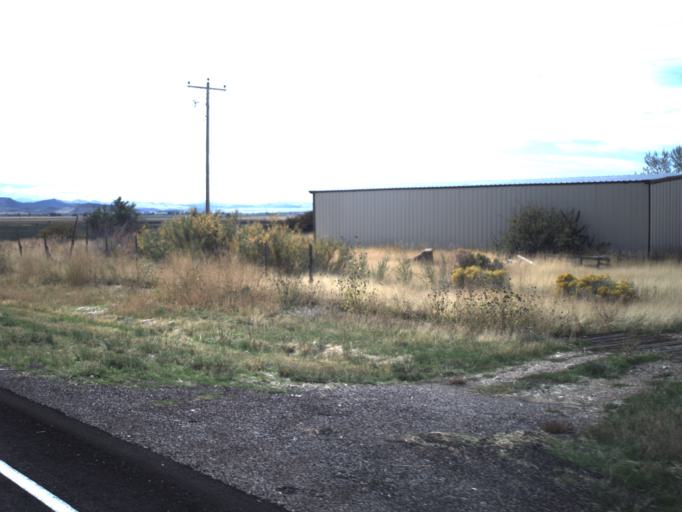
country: US
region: Utah
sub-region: Millard County
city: Fillmore
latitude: 38.8782
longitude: -112.4124
